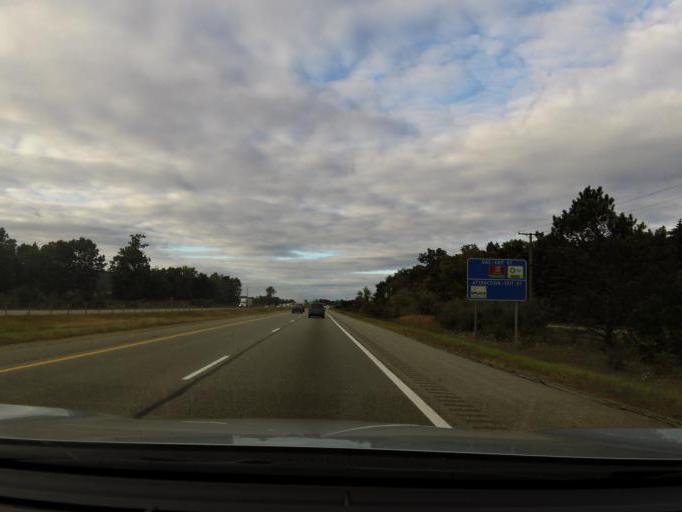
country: US
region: Michigan
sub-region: Livingston County
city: Brighton
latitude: 42.6242
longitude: -83.7485
